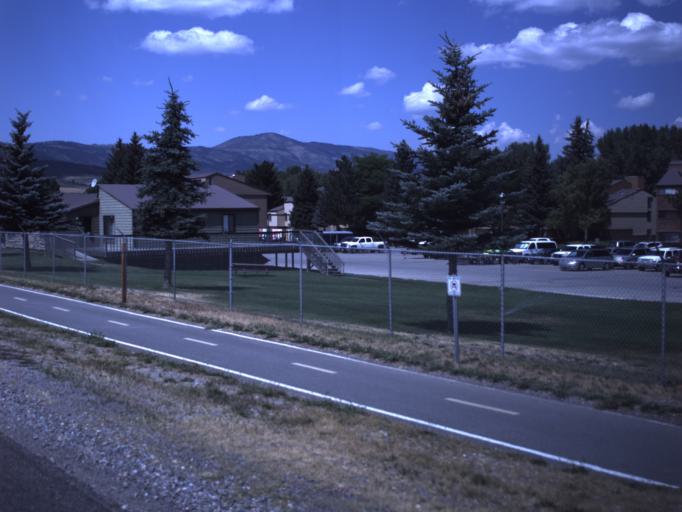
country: US
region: Utah
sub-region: Rich County
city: Randolph
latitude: 41.9065
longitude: -111.3803
